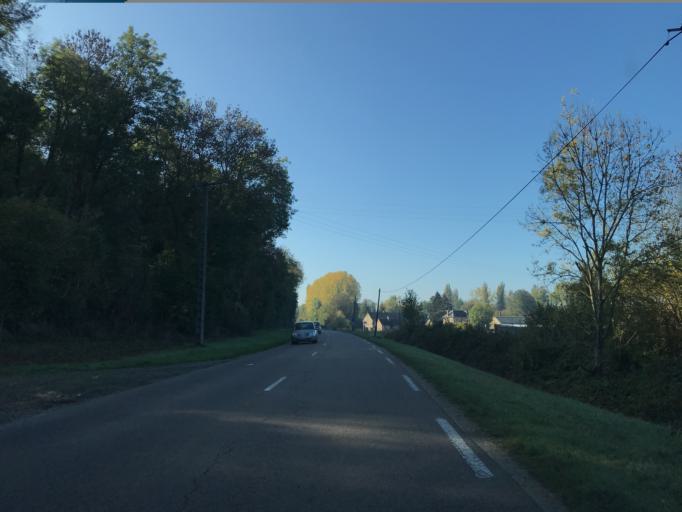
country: FR
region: Haute-Normandie
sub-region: Departement de l'Eure
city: Le Vaudreuil
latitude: 49.2409
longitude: 1.1940
